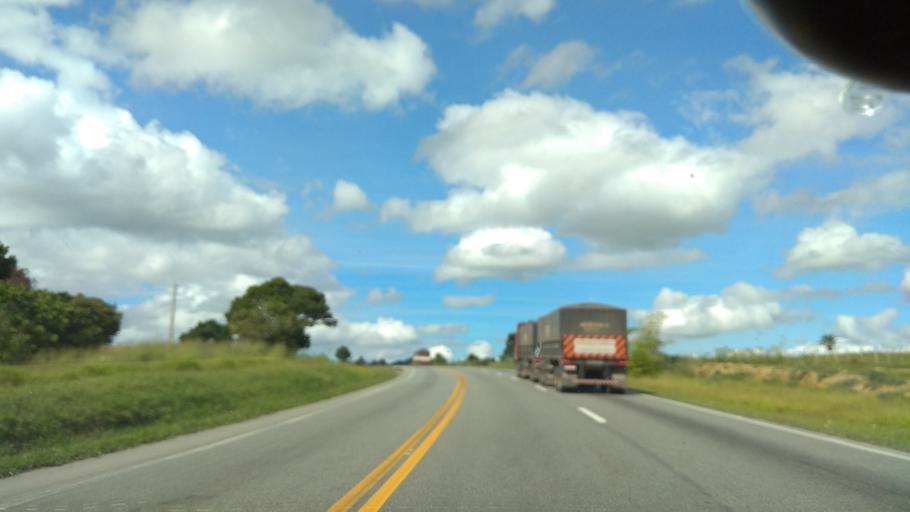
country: BR
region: Bahia
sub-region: Santa Ines
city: Santa Ines
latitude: -13.1074
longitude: -39.9775
